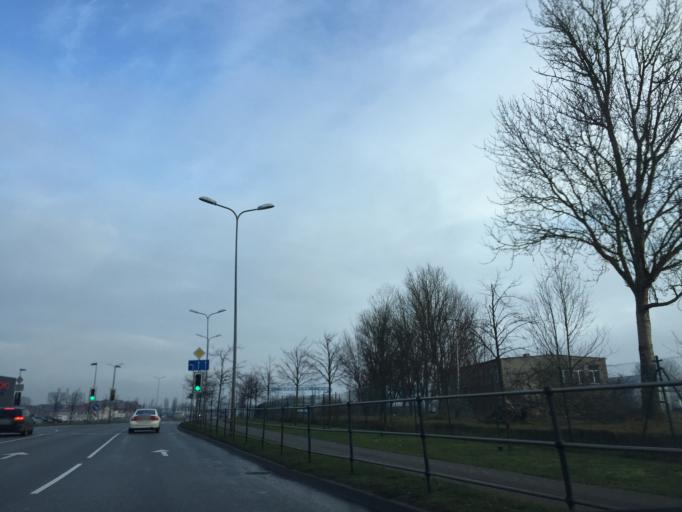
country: LV
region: Liepaja
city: Liepaja
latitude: 56.5160
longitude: 21.0238
